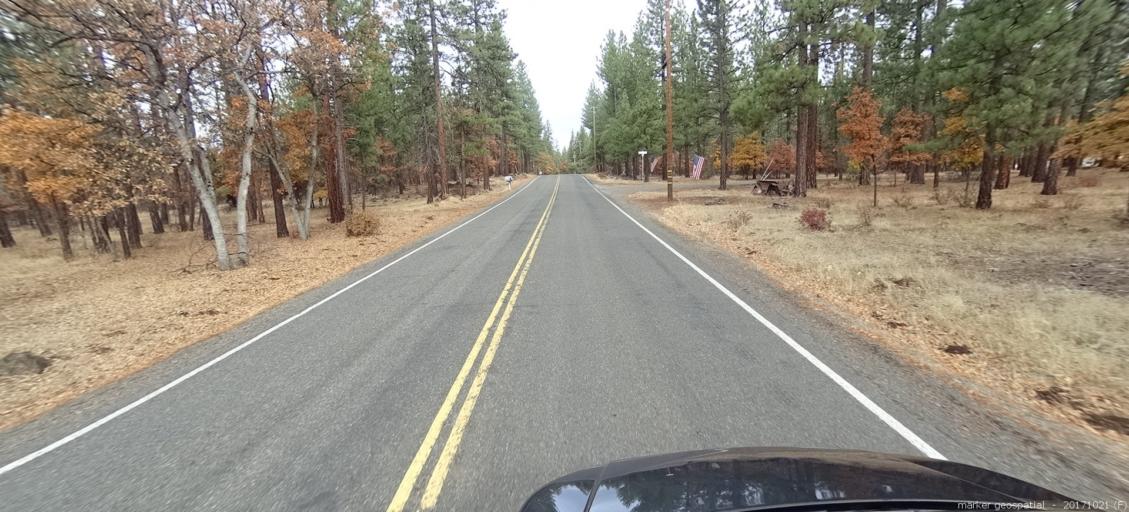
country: US
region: California
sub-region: Shasta County
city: Burney
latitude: 40.9503
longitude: -121.5730
